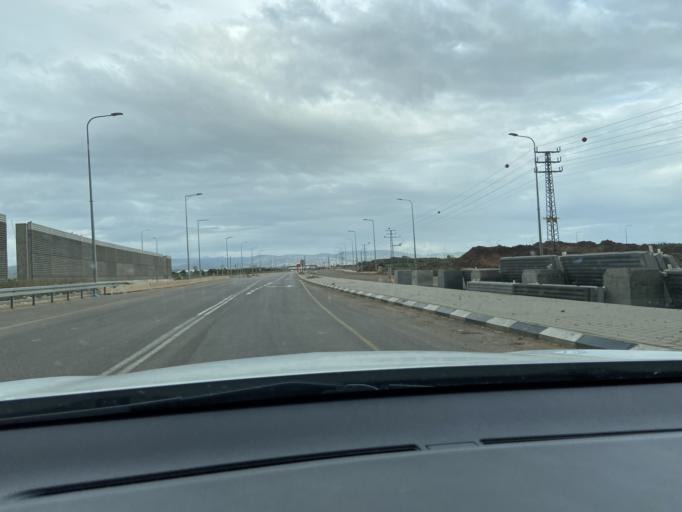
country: IL
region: Northern District
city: El Mazra`a
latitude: 32.9800
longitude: 35.1051
